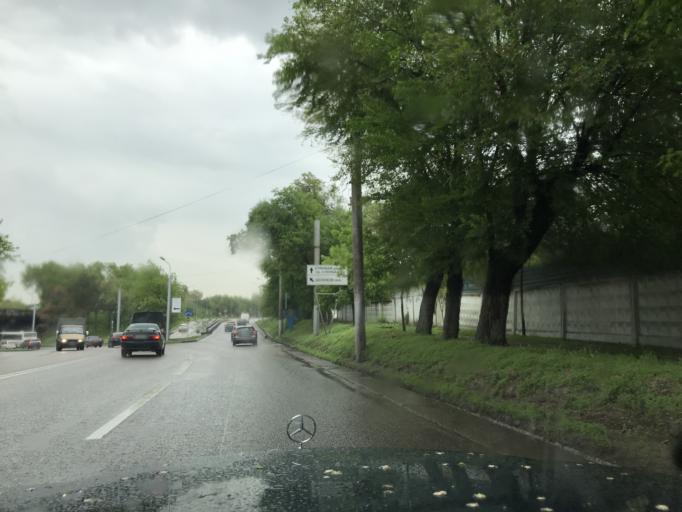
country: KZ
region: Almaty Oblysy
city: Pervomayskiy
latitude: 43.3306
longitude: 76.9601
